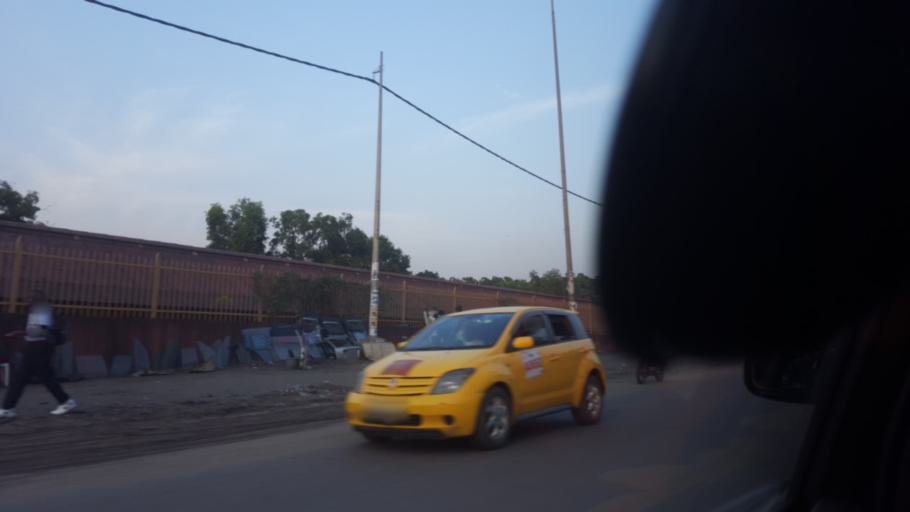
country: CD
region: Kinshasa
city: Kinshasa
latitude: -4.3429
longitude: 15.3202
